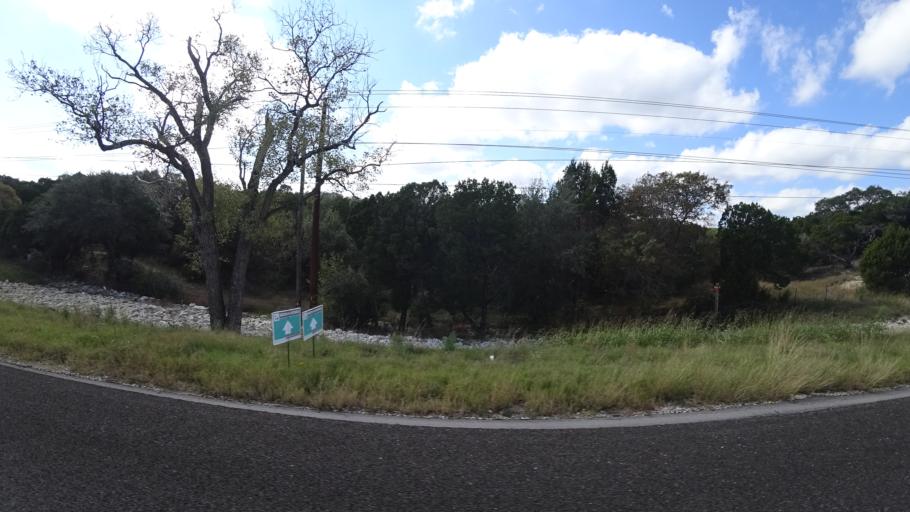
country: US
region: Texas
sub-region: Travis County
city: Barton Creek
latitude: 30.2687
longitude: -97.9101
